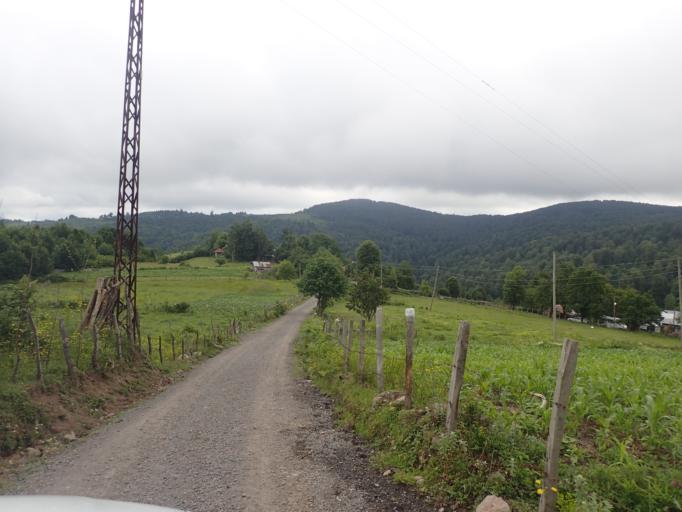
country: TR
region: Ordu
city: Akkus
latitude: 40.8596
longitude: 37.0153
